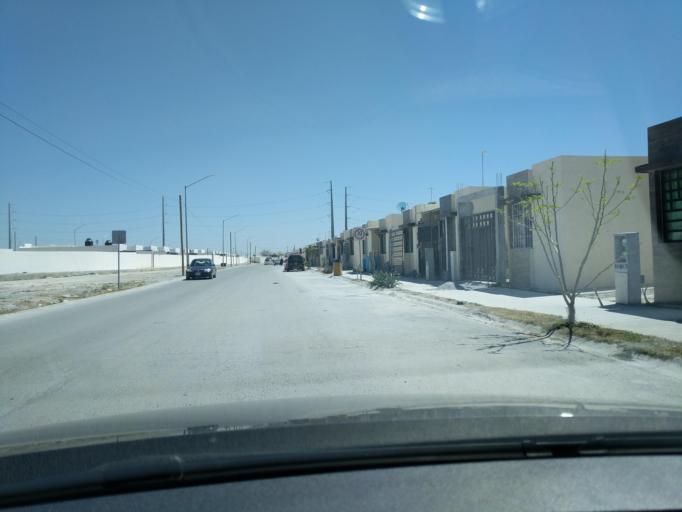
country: MX
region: Nuevo Leon
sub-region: Apodaca
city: Artemio Trevino
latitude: 25.8406
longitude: -100.1407
